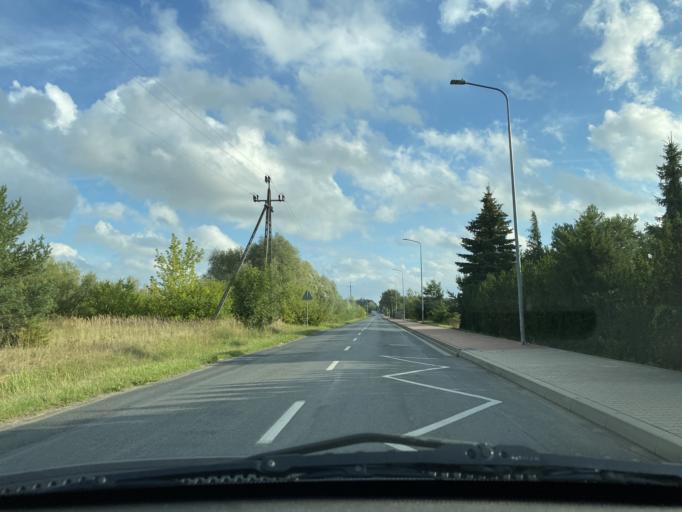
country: PL
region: Greater Poland Voivodeship
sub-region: Powiat poznanski
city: Baranowo
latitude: 52.4193
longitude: 16.7180
